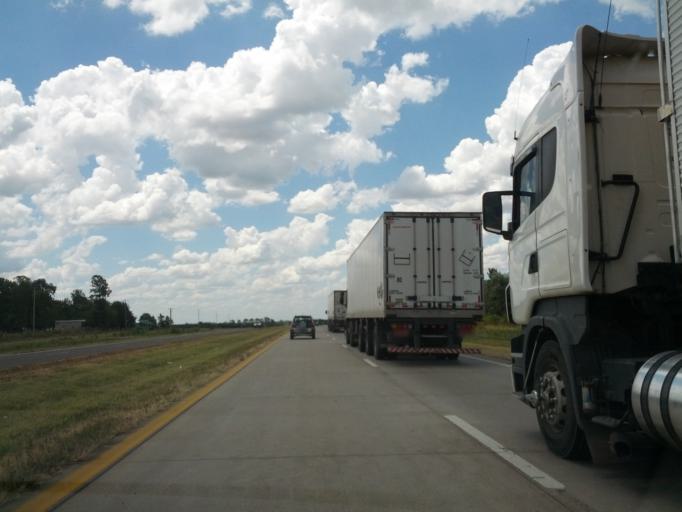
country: AR
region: Entre Rios
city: Gualeguaychu
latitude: -32.9971
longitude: -58.6005
